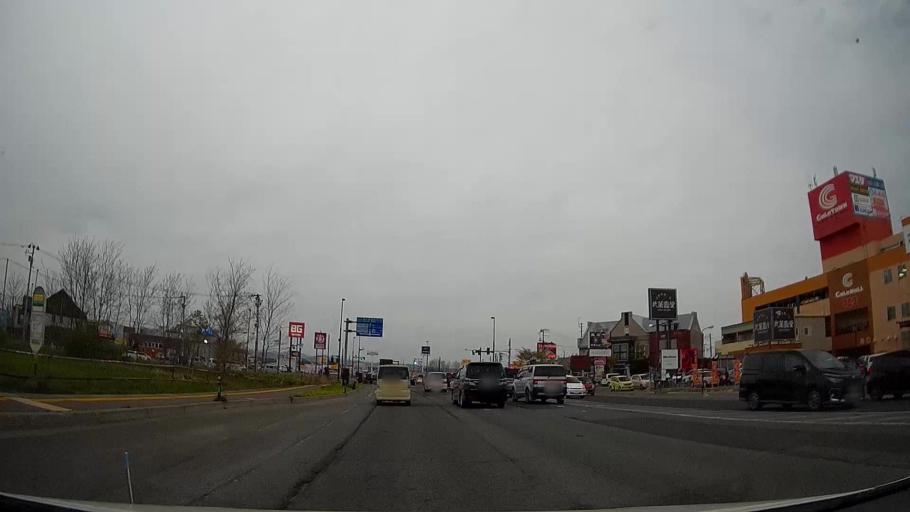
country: JP
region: Aomori
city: Aomori Shi
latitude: 40.8319
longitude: 140.7022
